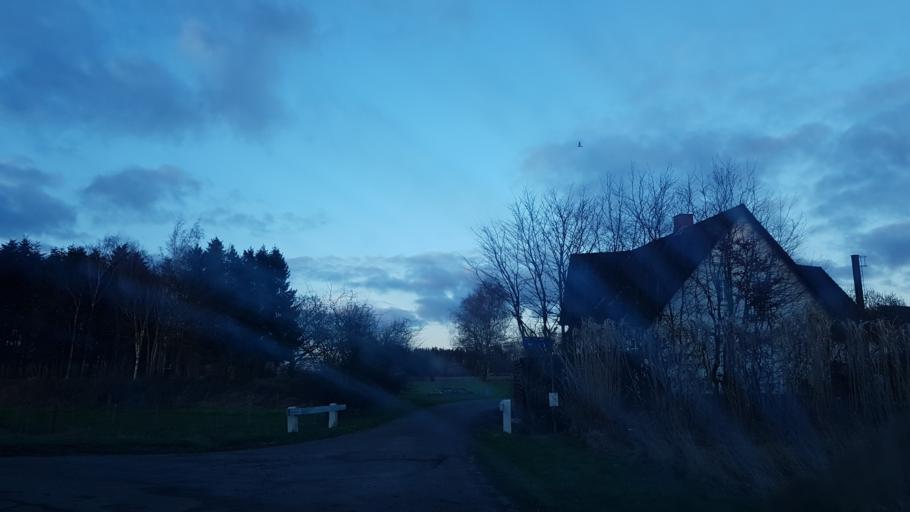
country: DK
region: South Denmark
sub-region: Kolding Kommune
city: Vamdrup
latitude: 55.3427
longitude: 9.2497
